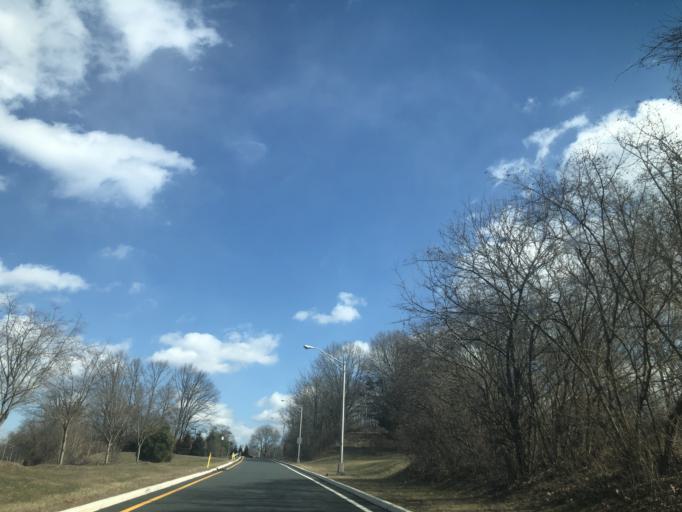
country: US
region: New Jersey
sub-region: Warren County
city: Belvidere
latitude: 40.9262
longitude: -75.0426
